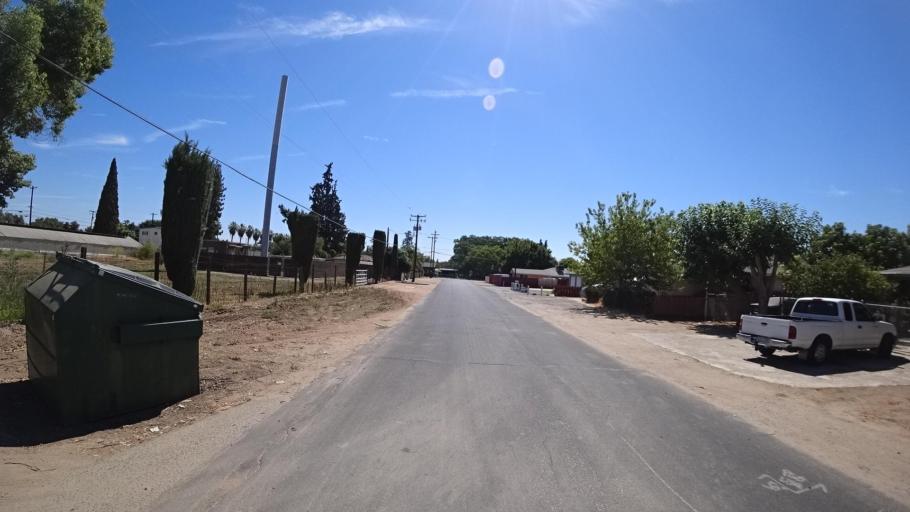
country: US
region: California
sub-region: Fresno County
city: Sunnyside
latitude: 36.7423
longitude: -119.7239
